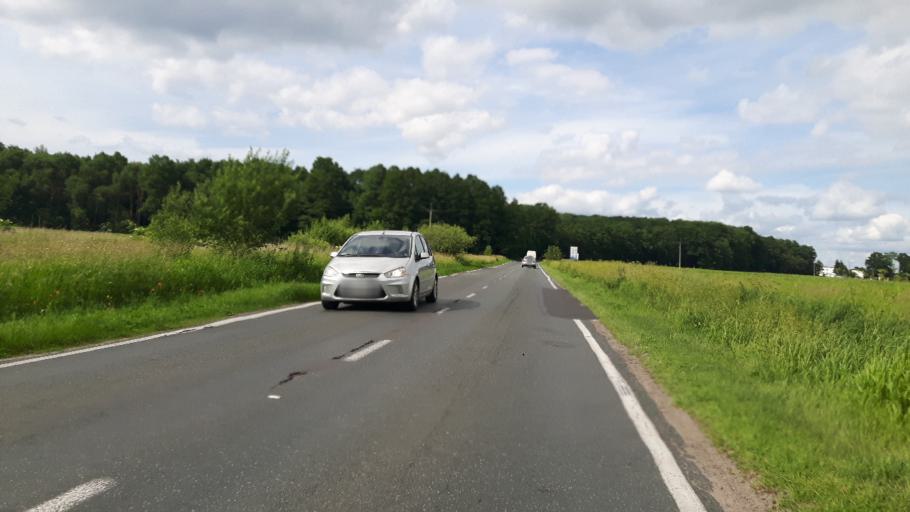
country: PL
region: West Pomeranian Voivodeship
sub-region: Powiat gryfinski
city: Stare Czarnowo
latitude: 53.4227
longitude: 14.7132
